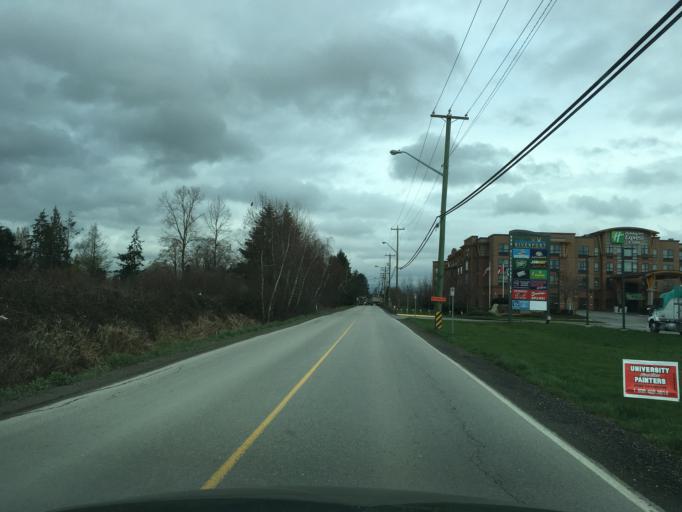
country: CA
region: British Columbia
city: Ladner
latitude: 49.1348
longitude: -123.0688
